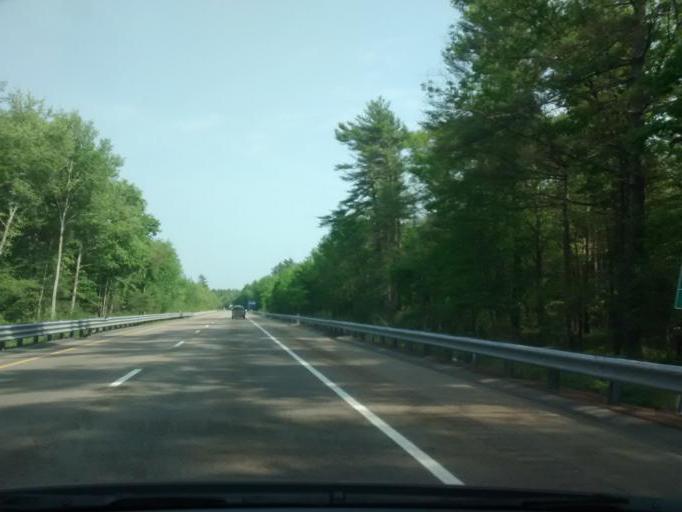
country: US
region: Massachusetts
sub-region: Plymouth County
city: West Wareham
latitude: 41.8189
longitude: -70.8018
